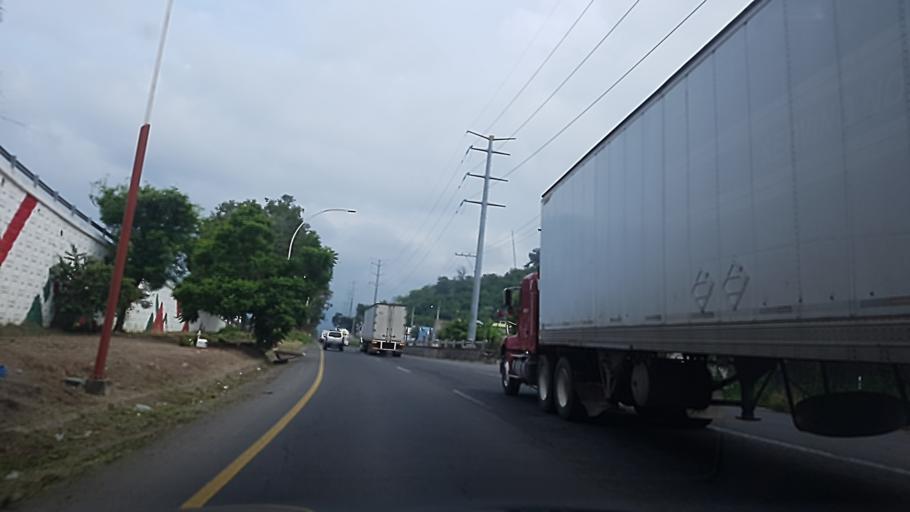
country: MX
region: Nayarit
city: Tepic
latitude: 21.4863
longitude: -104.9032
